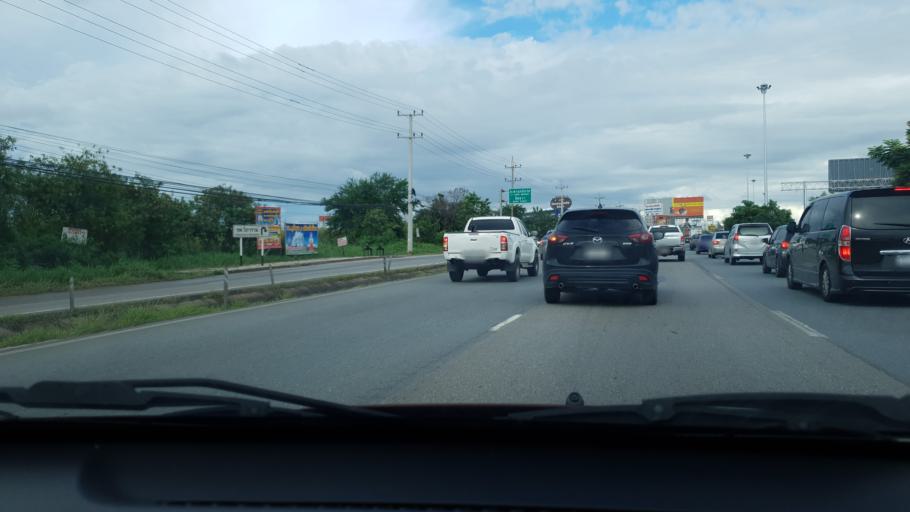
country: TH
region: Samut Sakhon
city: Samut Sakhon
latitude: 13.5655
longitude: 100.2798
